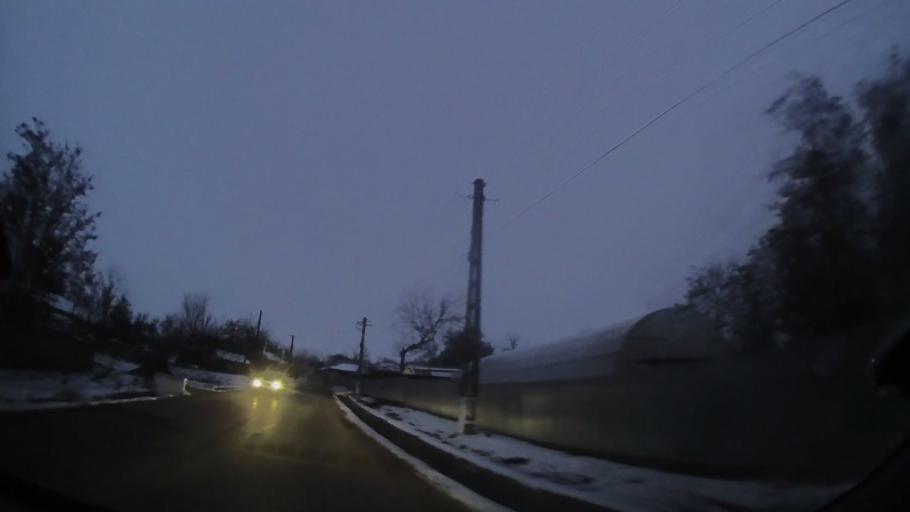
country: RO
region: Vaslui
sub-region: Comuna Dimitrie Cantemir
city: Dimitrie Cantemir
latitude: 46.5080
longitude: 28.0540
